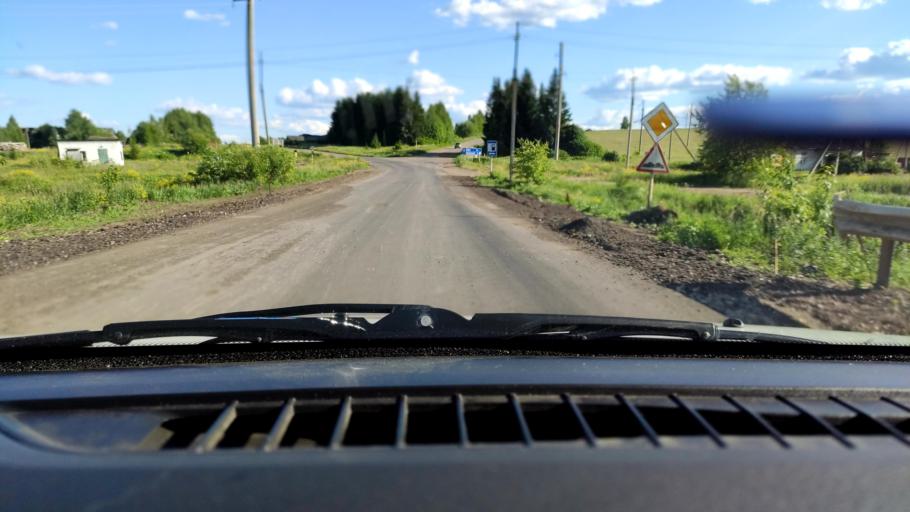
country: RU
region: Perm
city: Uinskoye
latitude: 57.1103
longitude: 56.5316
